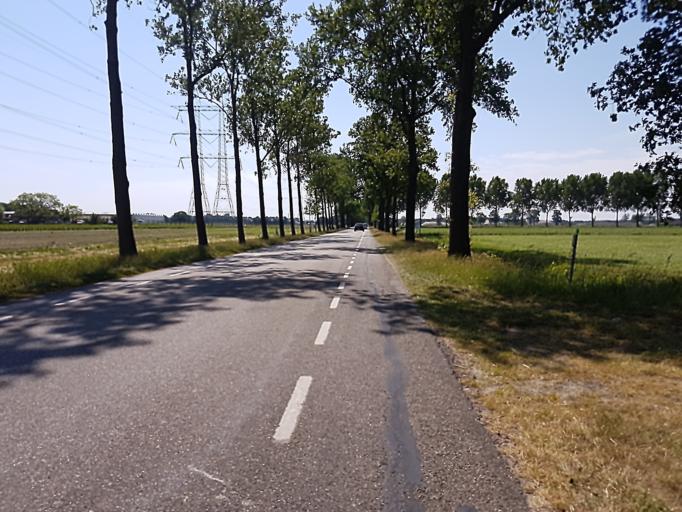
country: NL
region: North Brabant
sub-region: Gemeente Dongen
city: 's Gravenmoer
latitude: 51.6470
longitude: 4.9901
